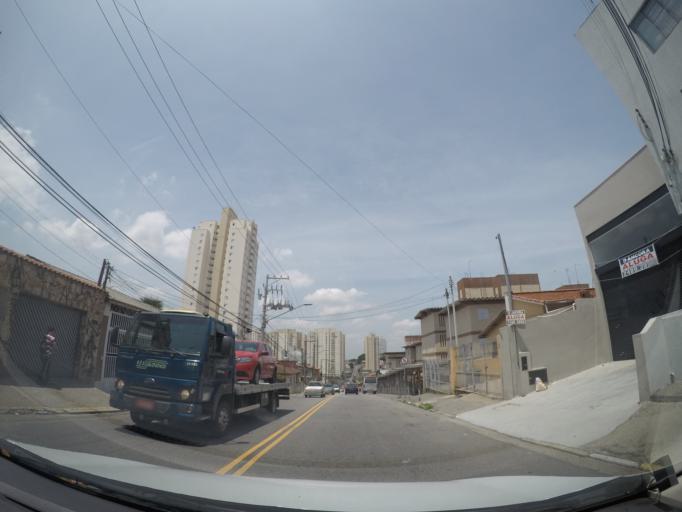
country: BR
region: Sao Paulo
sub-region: Guarulhos
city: Guarulhos
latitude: -23.4639
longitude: -46.5419
